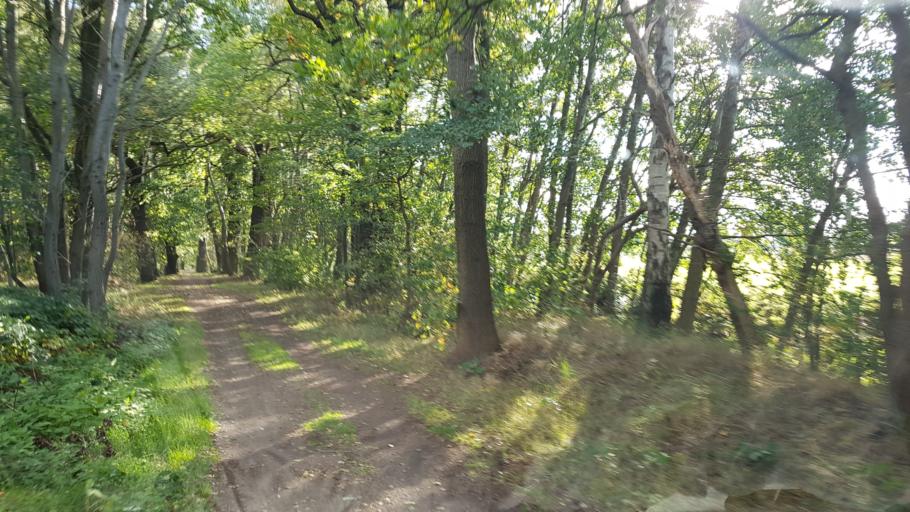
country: DE
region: Saxony
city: Dahlen
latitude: 51.3850
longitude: 12.9961
